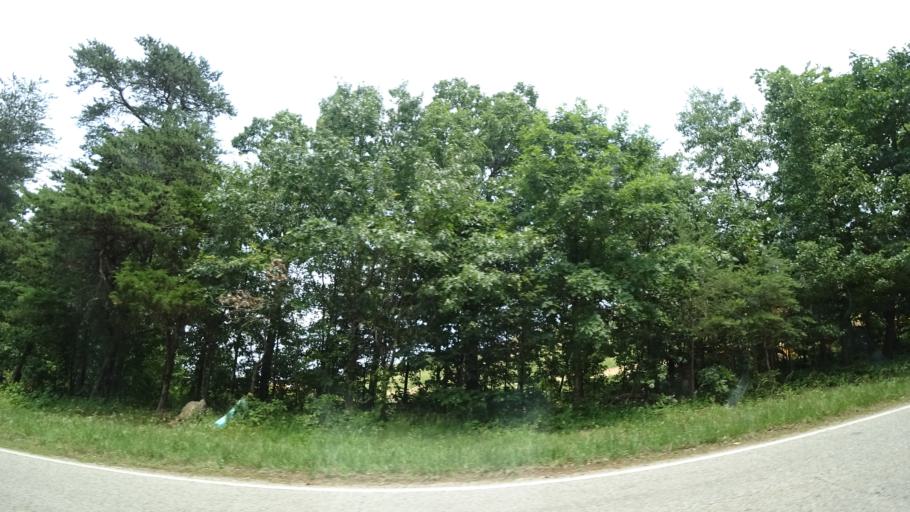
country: US
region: Virginia
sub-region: Fairfax County
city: Lorton
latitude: 38.6912
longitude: -77.2376
